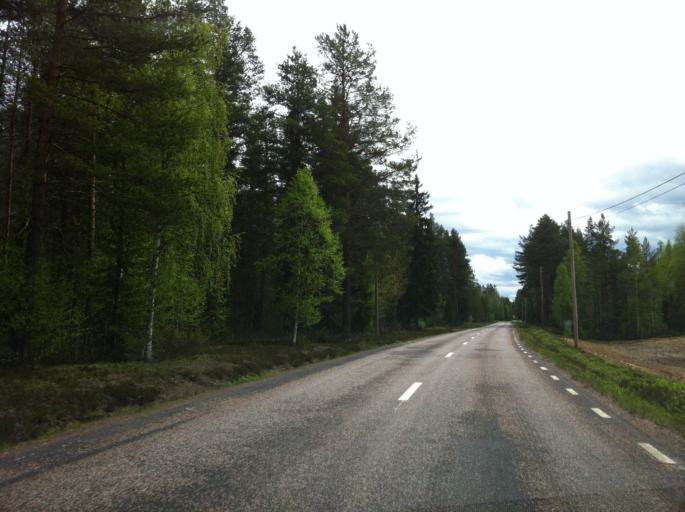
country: SE
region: Dalarna
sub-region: Malung-Saelens kommun
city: Malung
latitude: 61.2860
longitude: 13.1610
